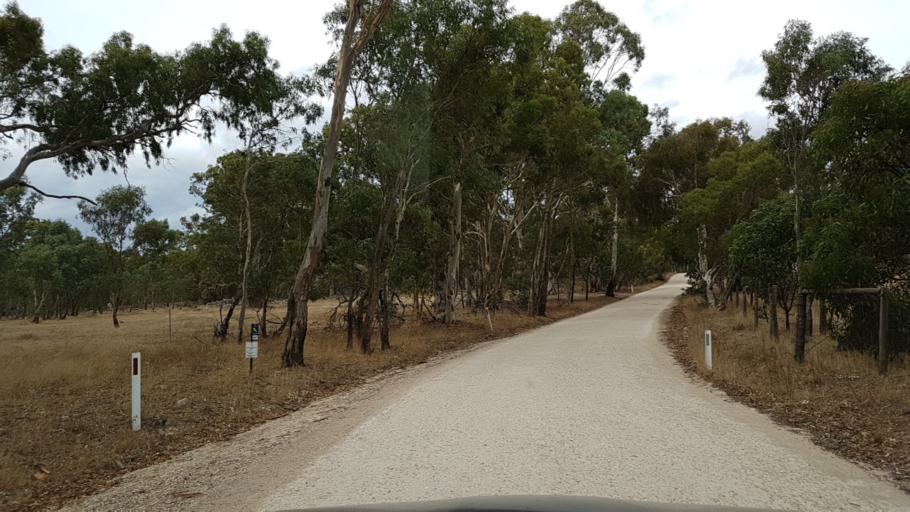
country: AU
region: South Australia
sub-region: Adelaide Hills
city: Birdwood
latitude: -34.7871
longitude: 138.9748
